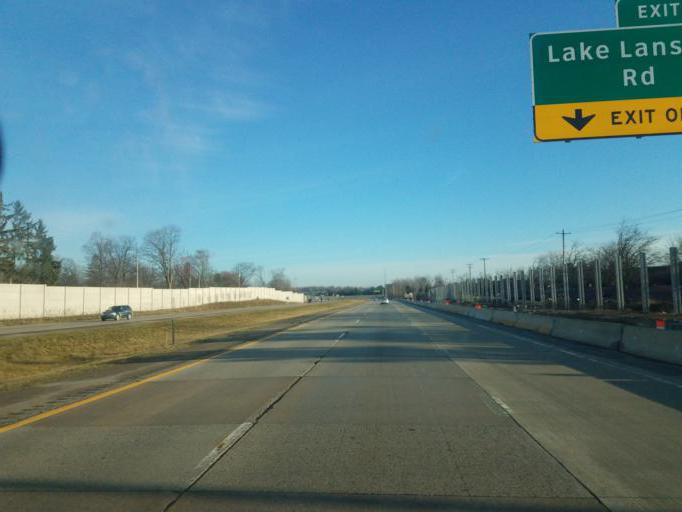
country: US
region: Michigan
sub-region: Ingham County
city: East Lansing
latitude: 42.7521
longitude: -84.5076
